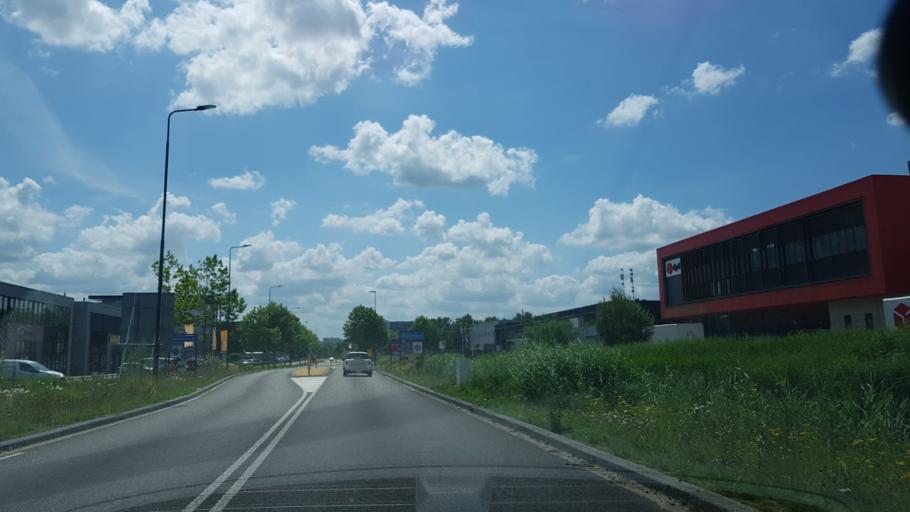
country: NL
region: Utrecht
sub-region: Gemeente Veenendaal
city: Veenendaal
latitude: 52.0465
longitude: 5.5657
